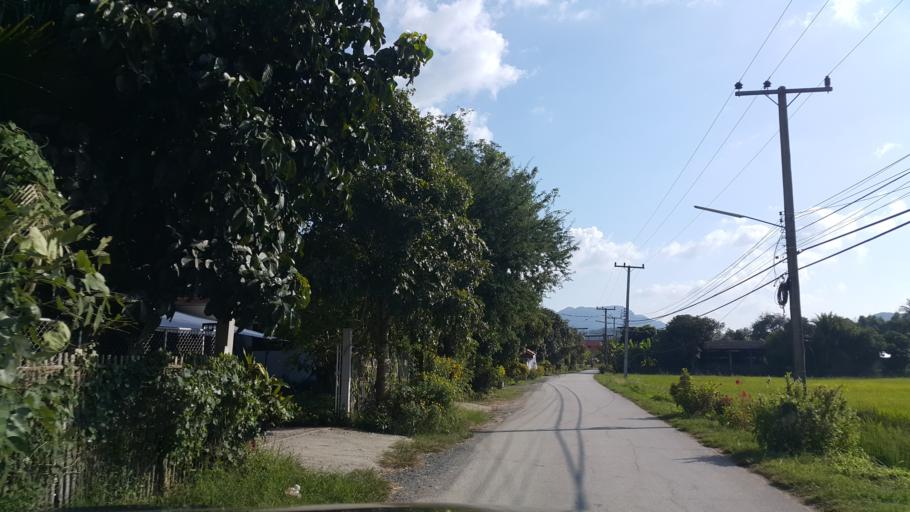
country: TH
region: Chiang Mai
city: Mae On
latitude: 18.7308
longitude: 99.2080
